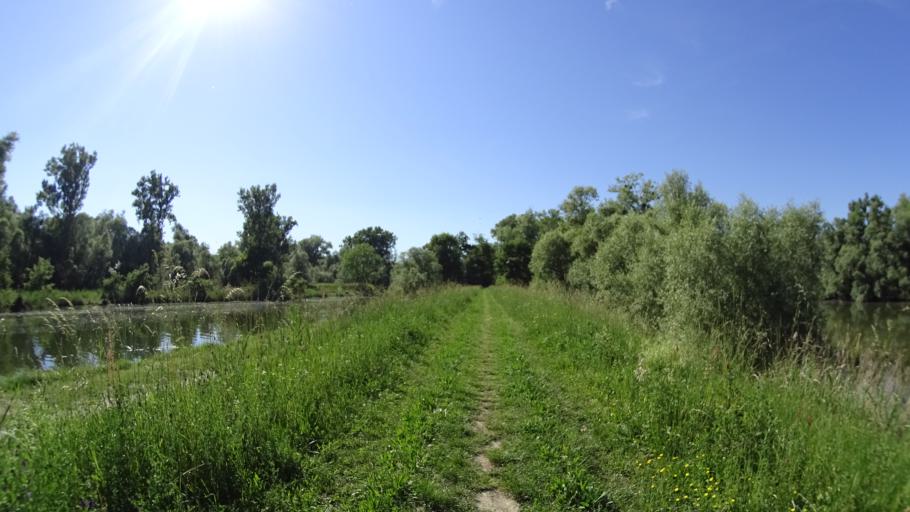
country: DE
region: Rheinland-Pfalz
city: Leimersheim
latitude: 49.1038
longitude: 8.3673
